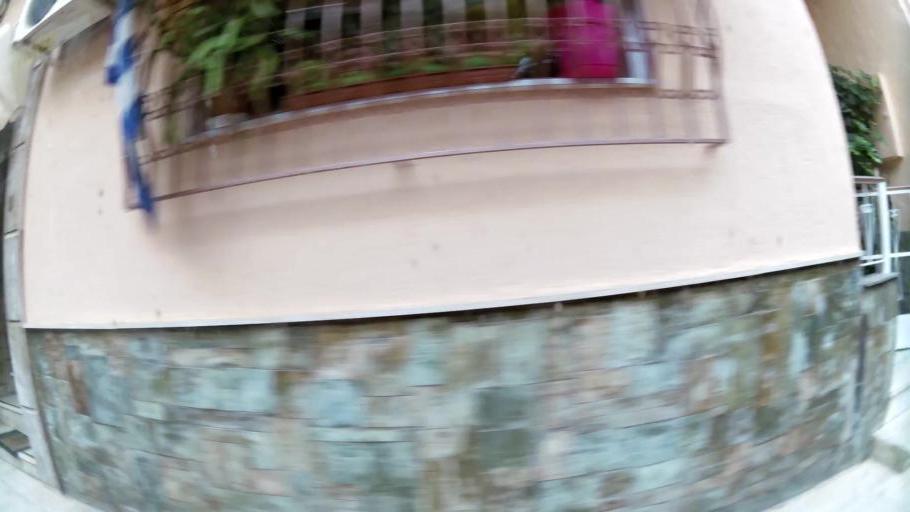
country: GR
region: Attica
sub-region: Nomarchia Athinas
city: Peristeri
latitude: 38.0091
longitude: 23.7086
